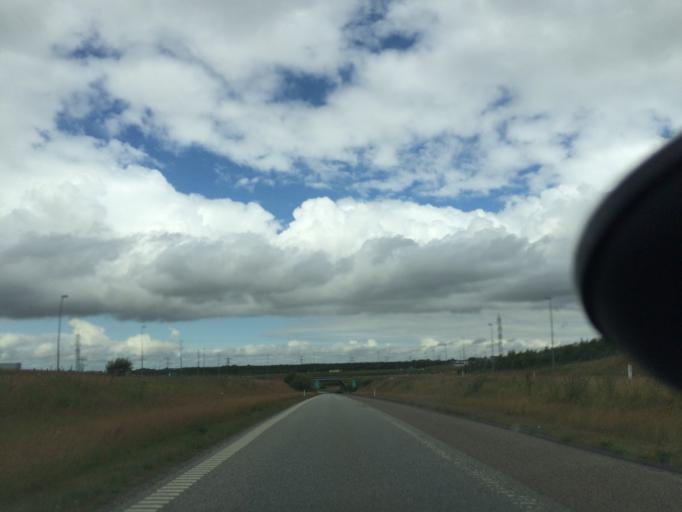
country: DK
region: Central Jutland
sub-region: Arhus Kommune
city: Kolt
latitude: 56.1548
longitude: 10.0729
